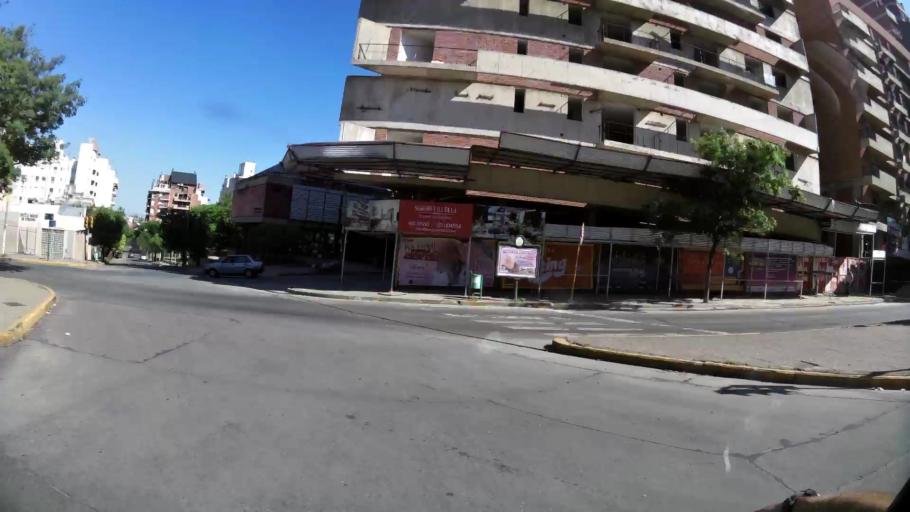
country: AR
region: Cordoba
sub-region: Departamento de Capital
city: Cordoba
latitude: -31.4310
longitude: -64.1901
